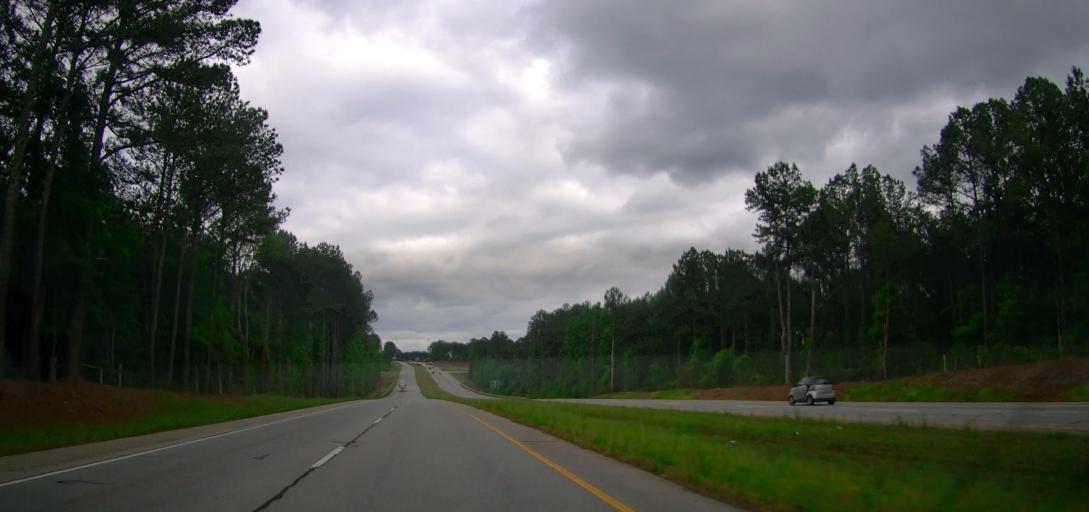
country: US
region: Georgia
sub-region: Walton County
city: Monroe
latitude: 33.8022
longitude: -83.7439
